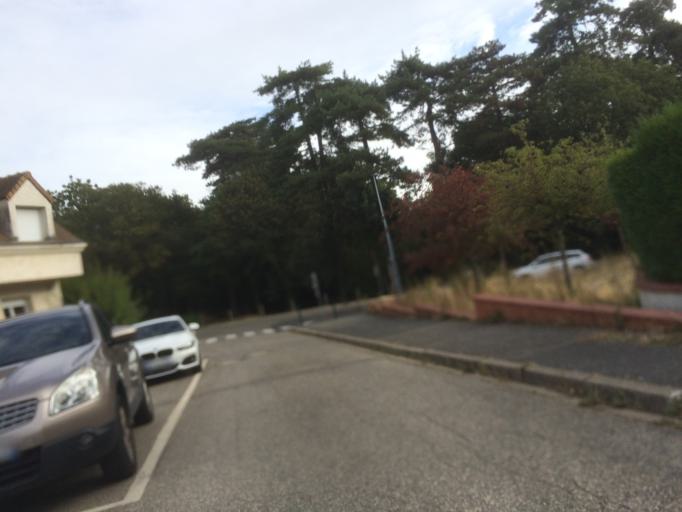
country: FR
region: Ile-de-France
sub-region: Departement de l'Essonne
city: Gometz-le-Chatel
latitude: 48.6749
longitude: 2.1386
